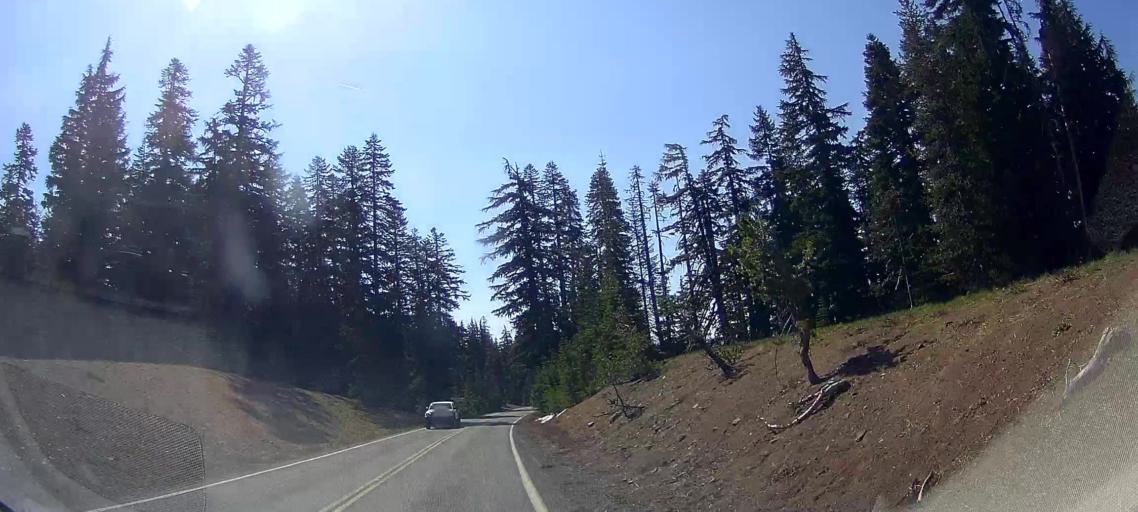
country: US
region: Oregon
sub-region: Klamath County
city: Klamath Falls
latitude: 42.8786
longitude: -122.1095
